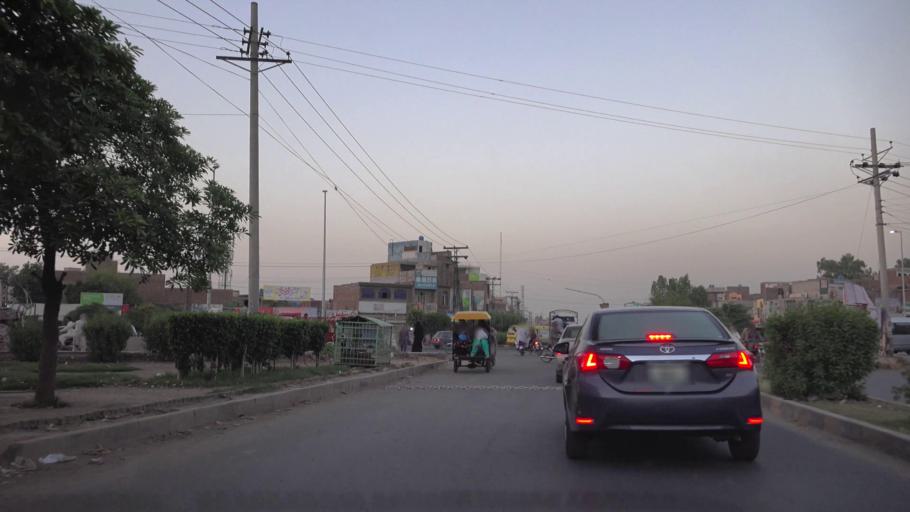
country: PK
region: Punjab
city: Faisalabad
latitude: 31.4524
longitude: 73.0986
